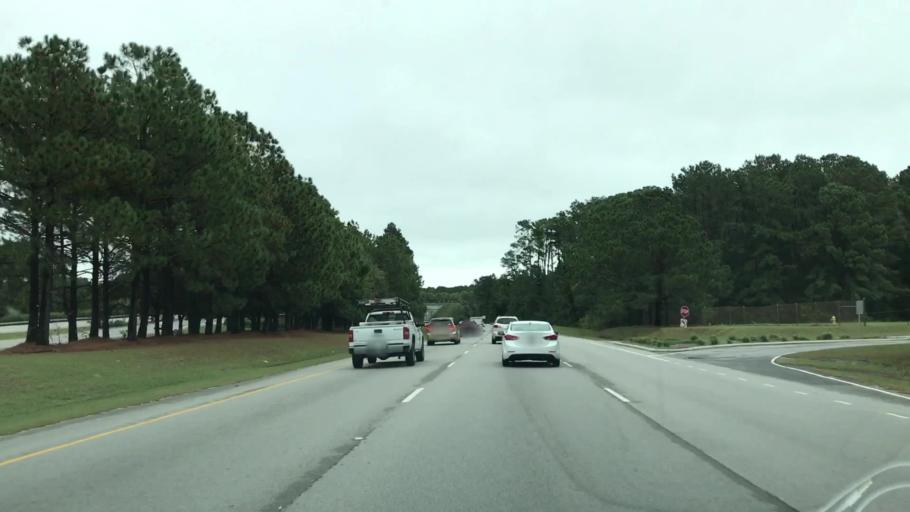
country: US
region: South Carolina
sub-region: Beaufort County
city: Hilton Head Island
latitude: 32.2151
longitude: -80.7435
